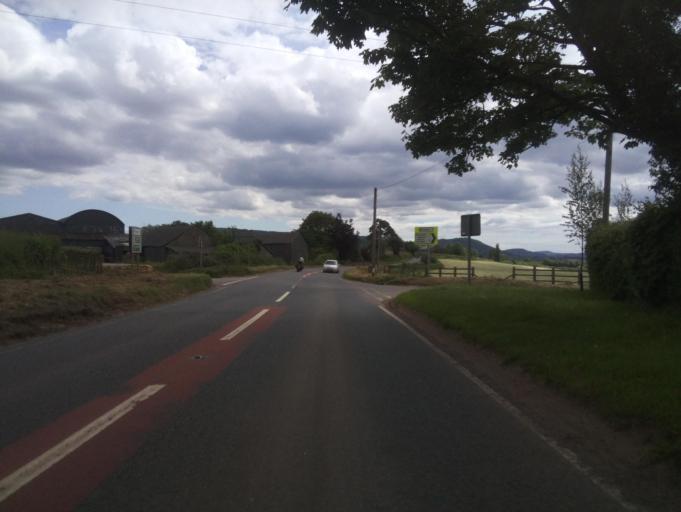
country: GB
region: England
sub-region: Herefordshire
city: Ross on Wye
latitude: 51.9353
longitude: -2.5595
